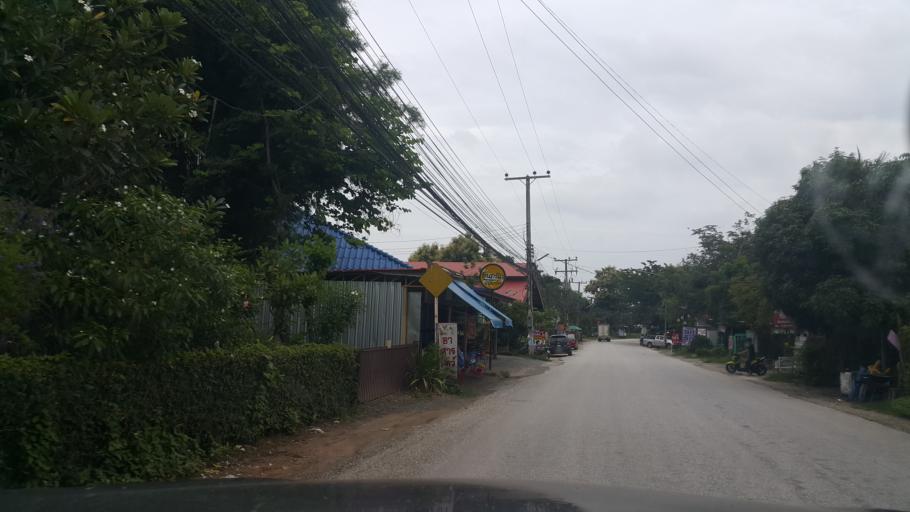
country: TH
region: Chiang Mai
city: San Sai
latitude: 18.9057
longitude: 99.0164
